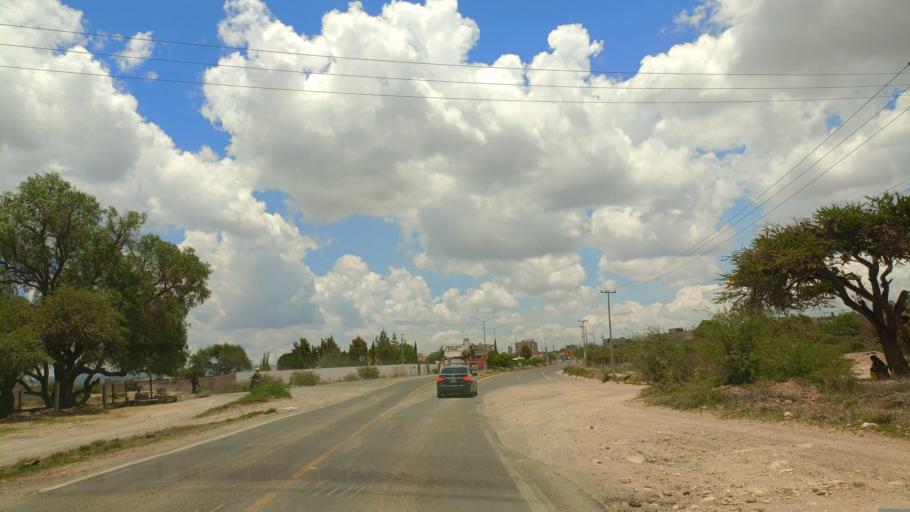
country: MX
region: Guerrero
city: San Luis de la Paz
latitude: 21.2846
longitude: -100.5049
